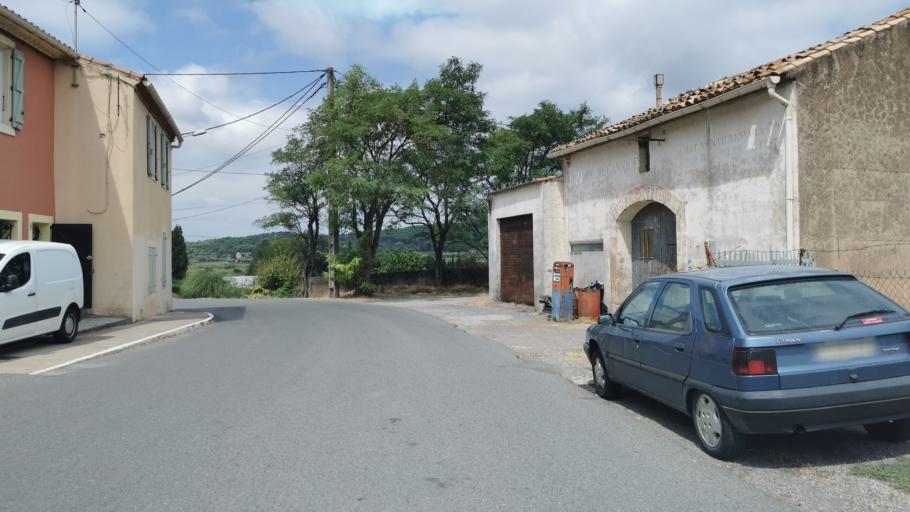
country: FR
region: Languedoc-Roussillon
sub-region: Departement de l'Aude
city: Bizanet
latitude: 43.1671
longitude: 2.8736
